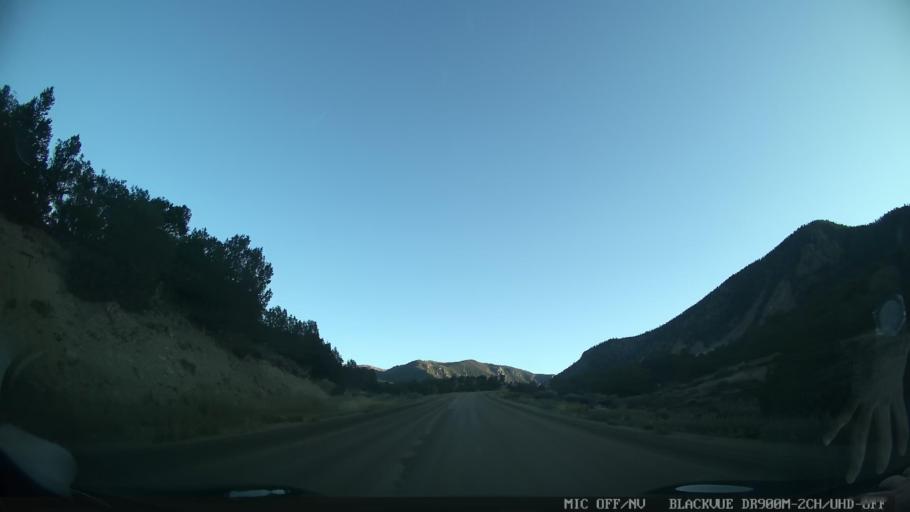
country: US
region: Colorado
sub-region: Grand County
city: Kremmling
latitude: 39.9813
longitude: -106.4970
